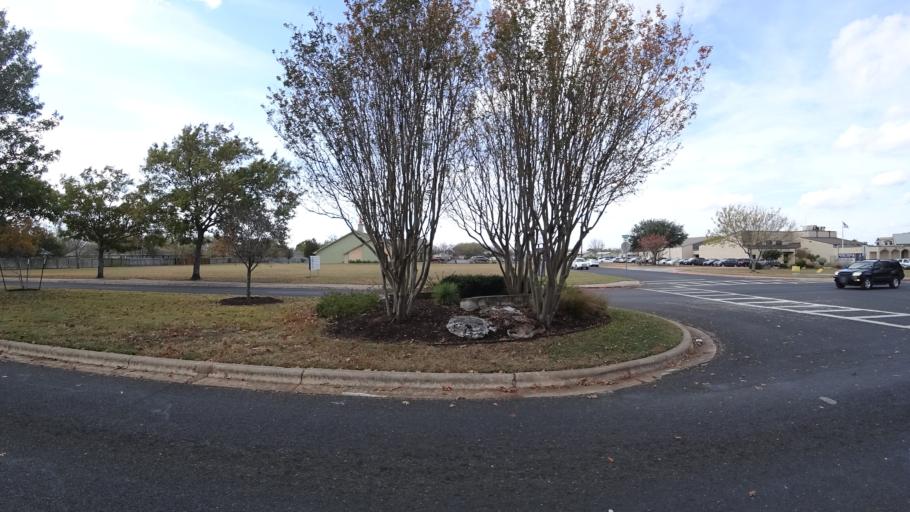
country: US
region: Texas
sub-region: Williamson County
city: Brushy Creek
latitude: 30.5105
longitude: -97.7368
